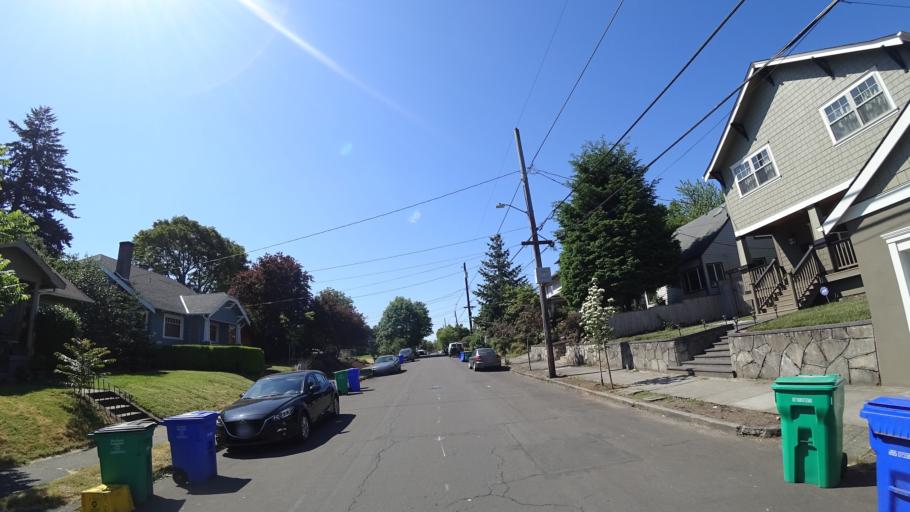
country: US
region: Oregon
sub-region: Multnomah County
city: Portland
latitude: 45.5611
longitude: -122.6488
